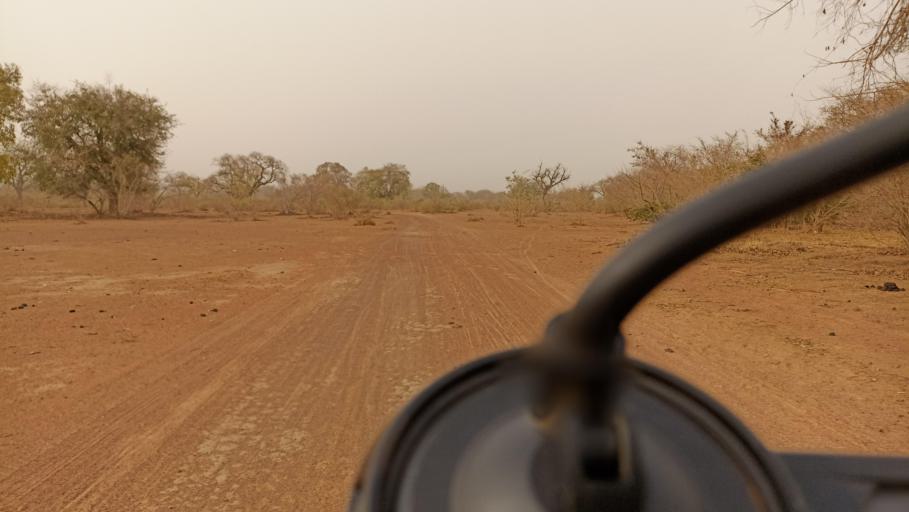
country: BF
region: Nord
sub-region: Province du Zondoma
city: Gourcy
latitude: 13.1705
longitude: -2.5883
